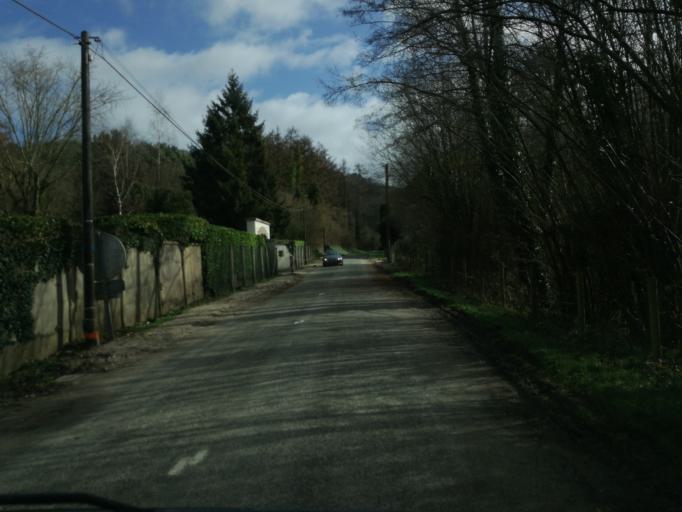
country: FR
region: Haute-Normandie
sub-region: Departement de la Seine-Maritime
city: Bretteville-du-Grand-Caux
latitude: 49.7065
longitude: 0.4353
